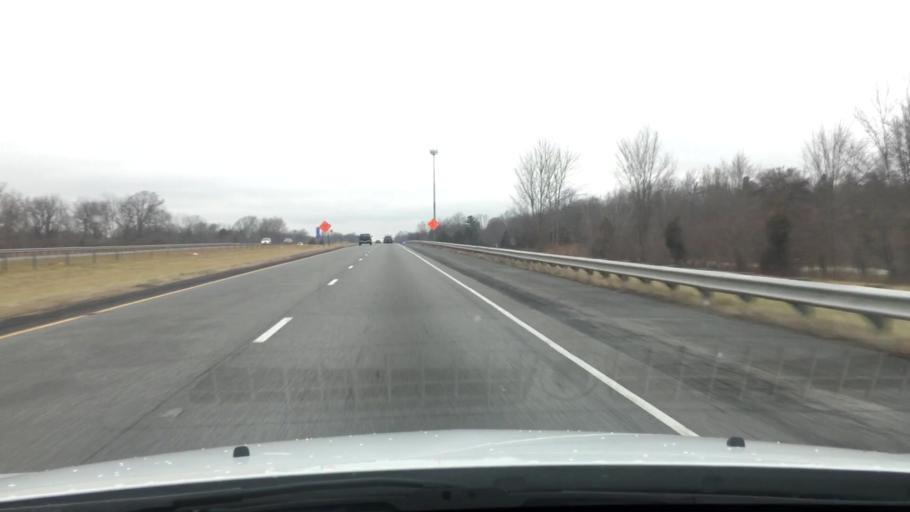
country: US
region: Indiana
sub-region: Boone County
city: Zionsville
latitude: 39.9186
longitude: -86.3286
